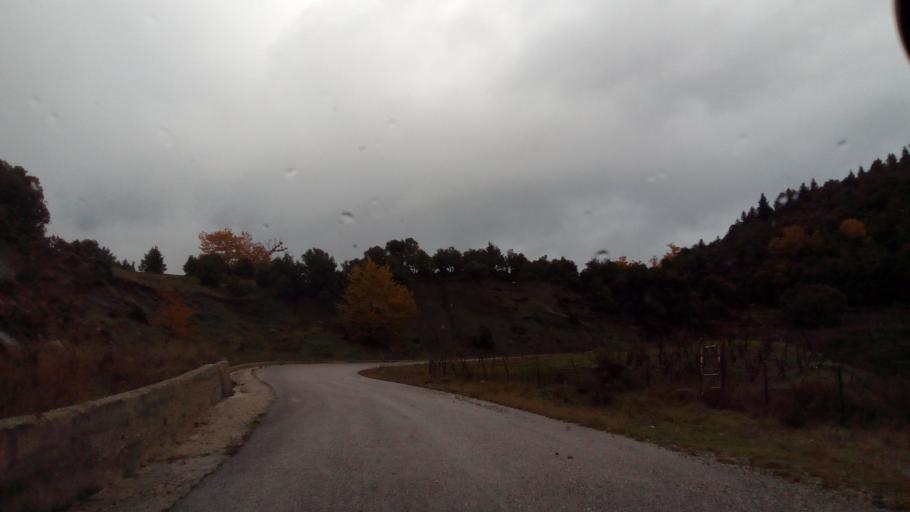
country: GR
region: West Greece
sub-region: Nomos Aitolias kai Akarnanias
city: Thermo
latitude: 38.6814
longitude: 21.8549
